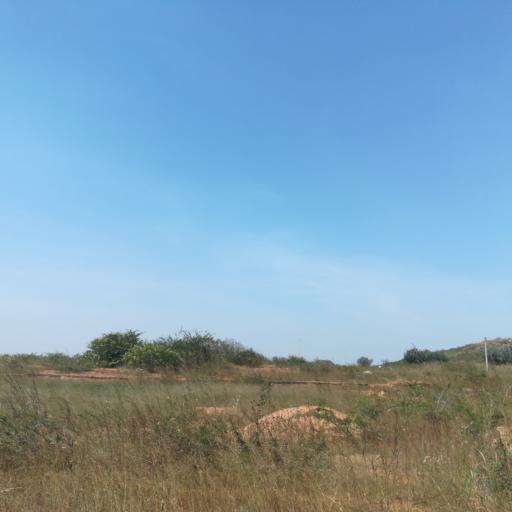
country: NG
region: Plateau
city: Bukuru
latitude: 9.8471
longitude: 8.9202
